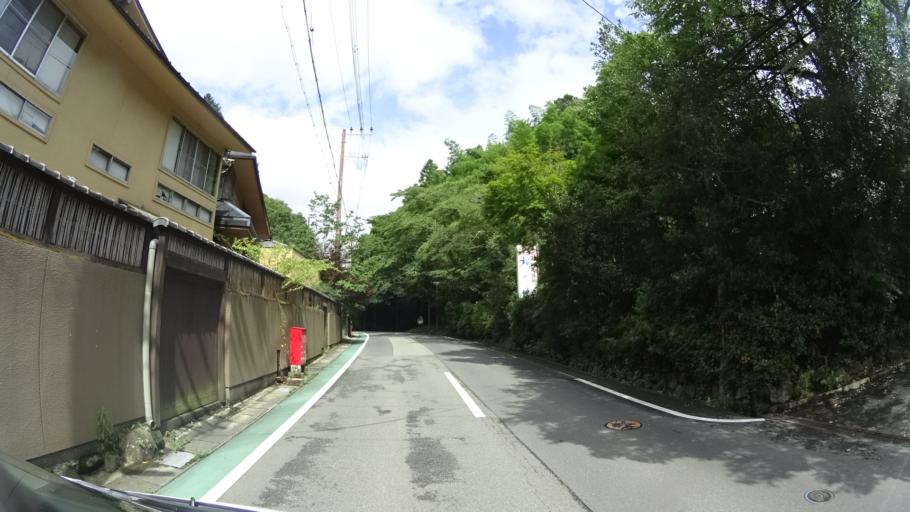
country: JP
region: Kyoto
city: Kameoka
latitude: 35.0198
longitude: 135.5145
